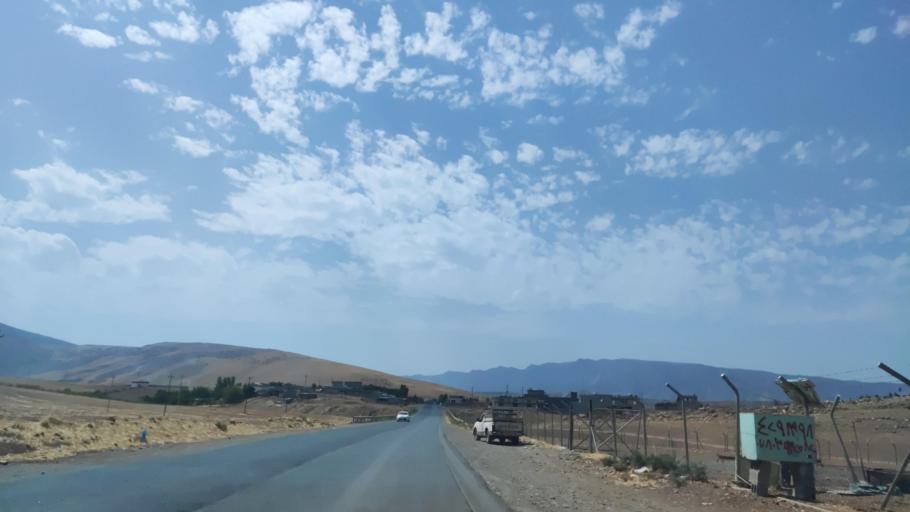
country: IQ
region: Arbil
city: Shaqlawah
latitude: 36.4817
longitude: 44.3978
